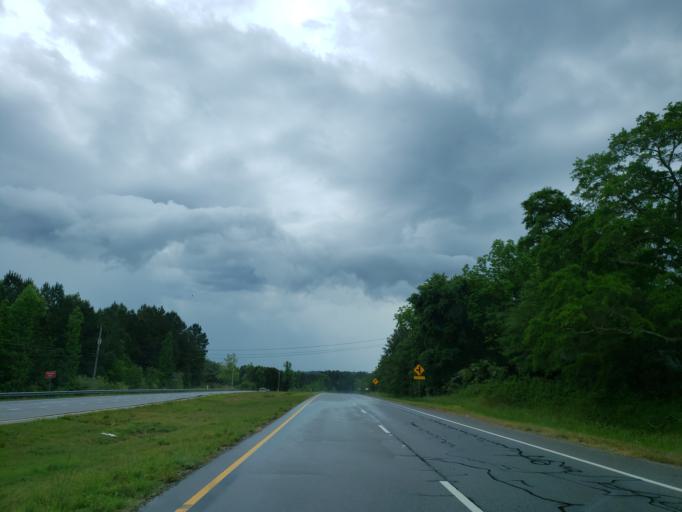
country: US
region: Georgia
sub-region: Haralson County
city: Buchanan
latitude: 33.8714
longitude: -85.2170
